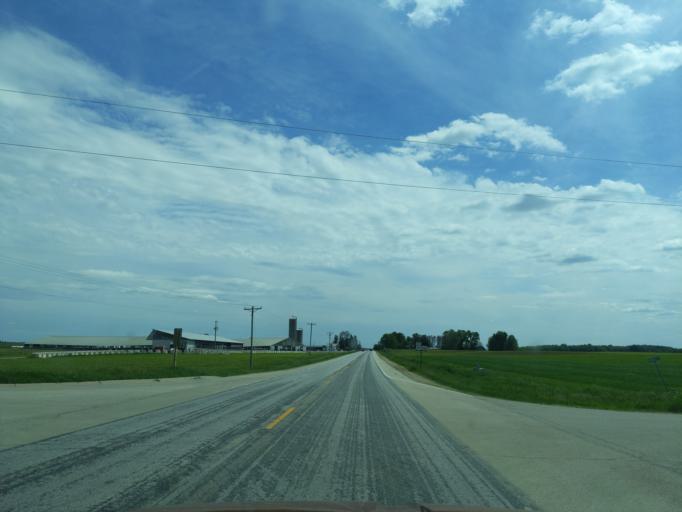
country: US
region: Wisconsin
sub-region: Dane County
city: De Forest
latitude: 43.2957
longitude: -89.3247
